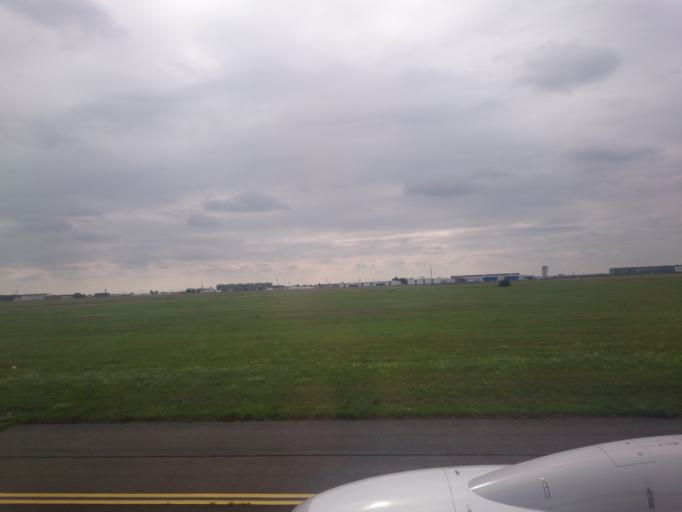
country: DE
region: Brandenburg
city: Schonefeld
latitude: 52.3796
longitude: 13.5103
